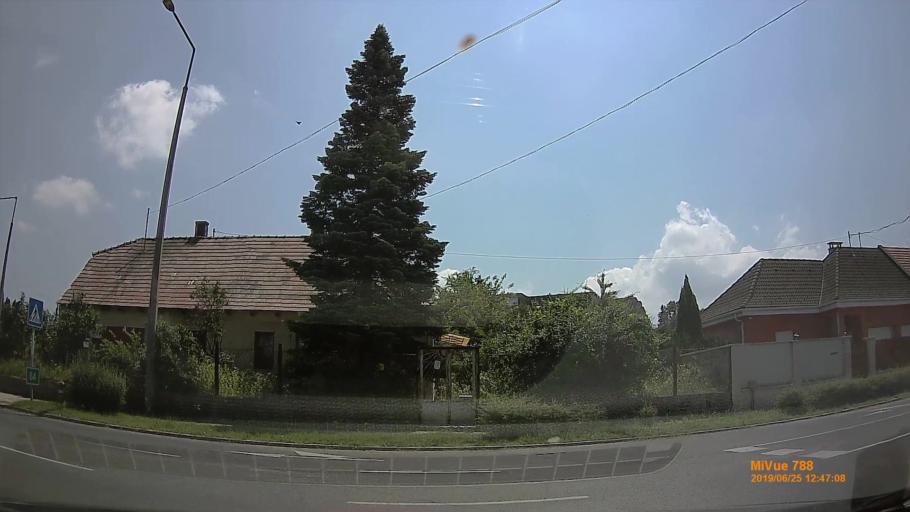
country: HU
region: Komarom-Esztergom
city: Esztergom
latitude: 47.8040
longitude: 18.7502
